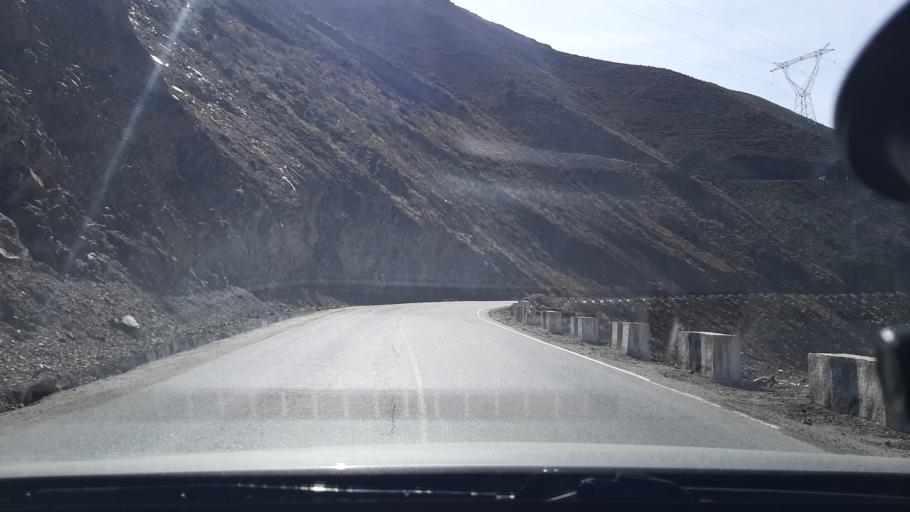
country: TJ
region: Viloyati Sughd
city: Ayni
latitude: 39.4419
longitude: 68.5475
